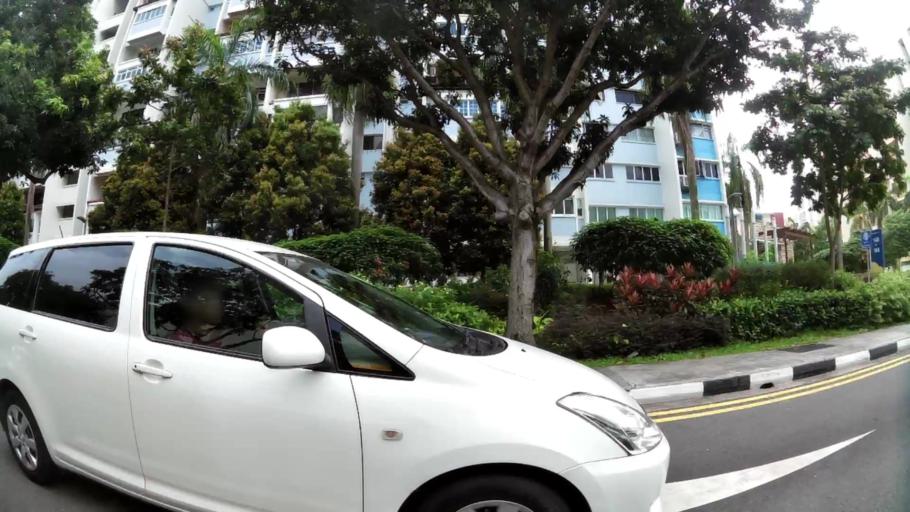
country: SG
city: Singapore
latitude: 1.3517
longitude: 103.9447
